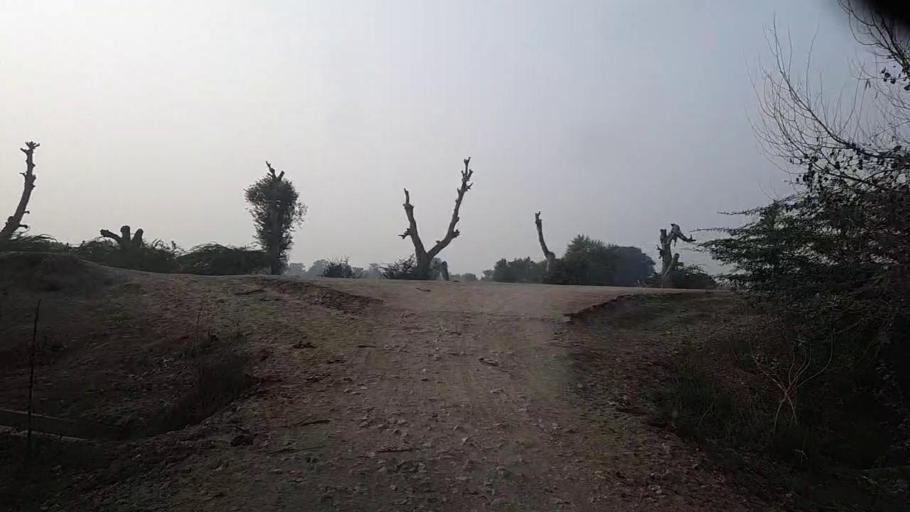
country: PK
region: Sindh
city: Bozdar
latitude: 27.1505
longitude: 68.6614
